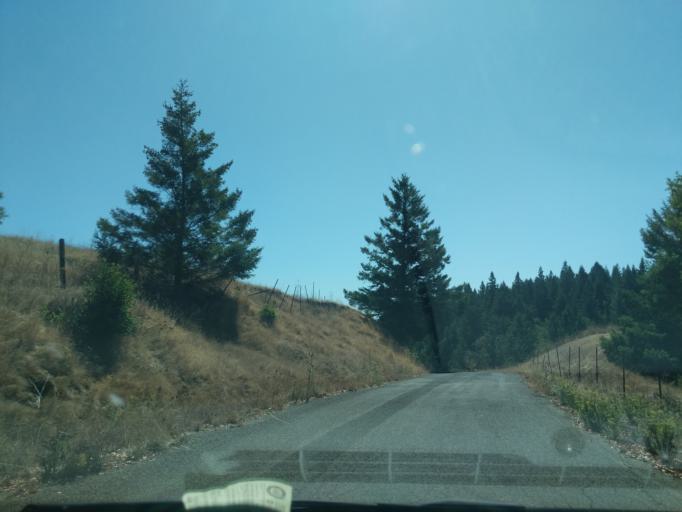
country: US
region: California
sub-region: Sonoma County
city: Monte Rio
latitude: 38.5289
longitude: -123.2262
